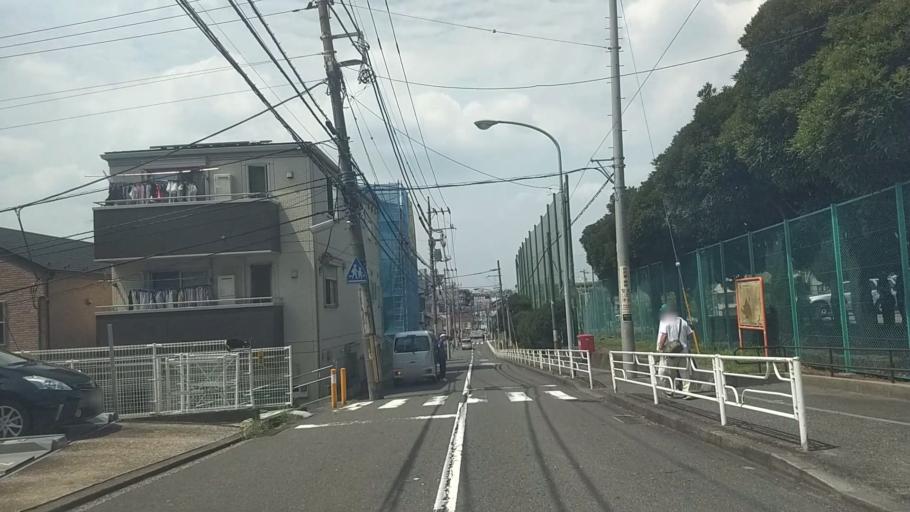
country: JP
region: Kanagawa
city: Yokohama
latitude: 35.4942
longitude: 139.6527
